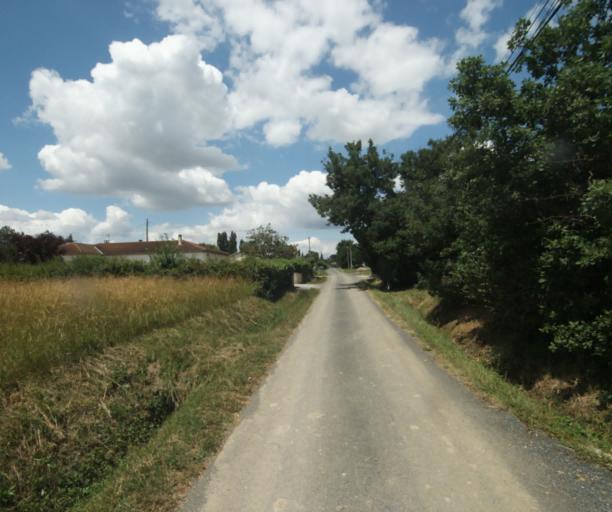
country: FR
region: Midi-Pyrenees
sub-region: Departement du Tarn
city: Soual
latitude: 43.5378
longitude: 2.0635
